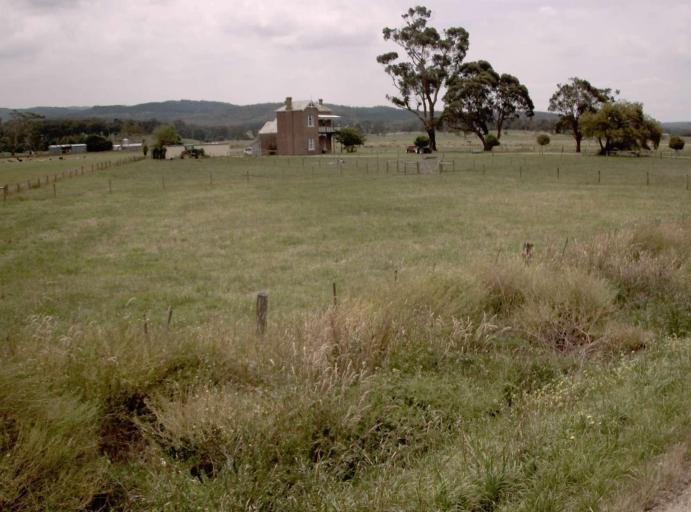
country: AU
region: Victoria
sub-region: Latrobe
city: Traralgon
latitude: -38.5001
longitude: 146.6724
